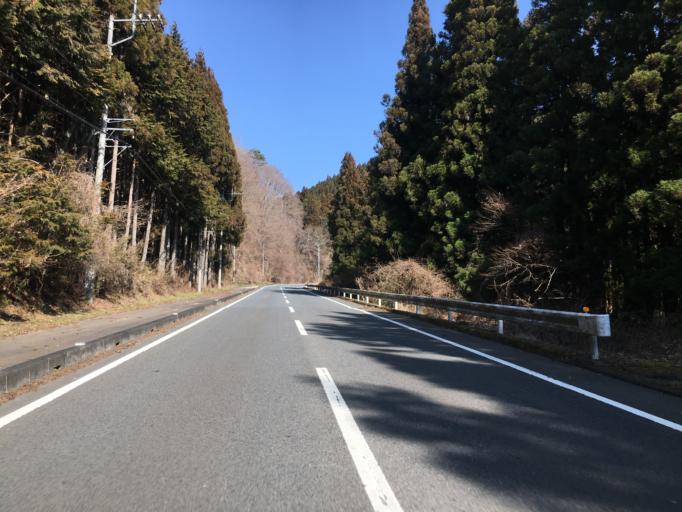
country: JP
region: Ibaraki
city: Daigo
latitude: 36.7955
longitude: 140.4868
